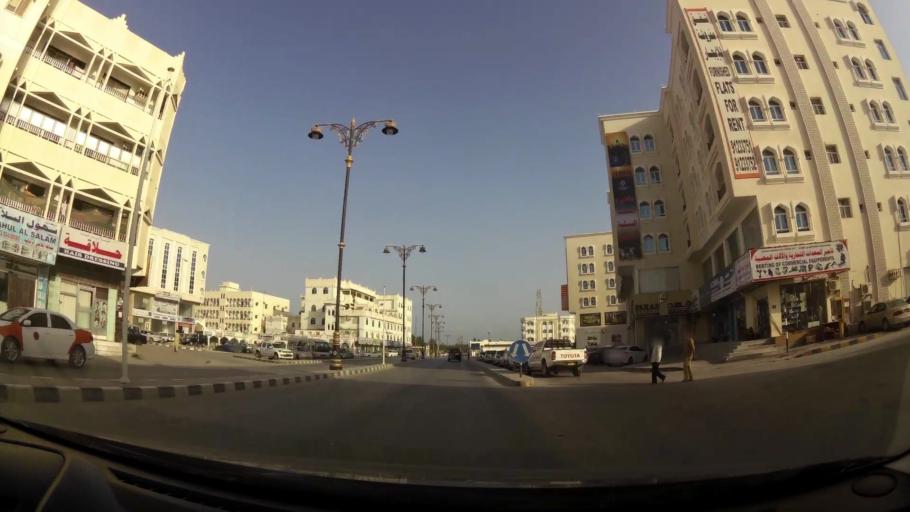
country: OM
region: Zufar
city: Salalah
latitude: 17.0114
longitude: 54.0942
